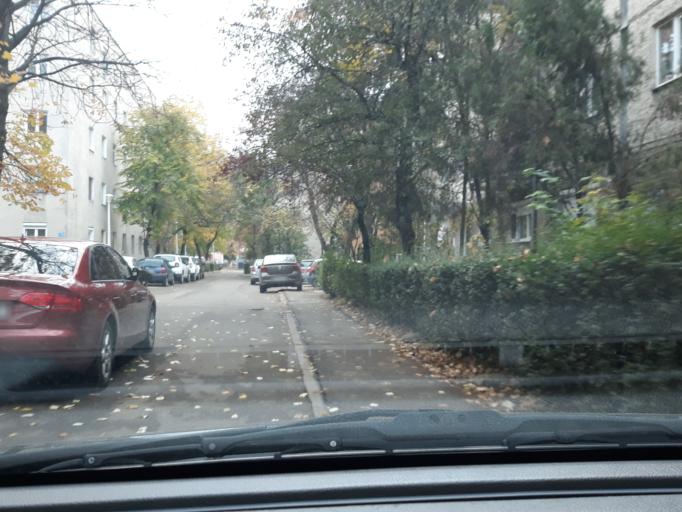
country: RO
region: Bihor
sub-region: Comuna Biharea
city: Oradea
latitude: 47.0738
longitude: 21.9193
